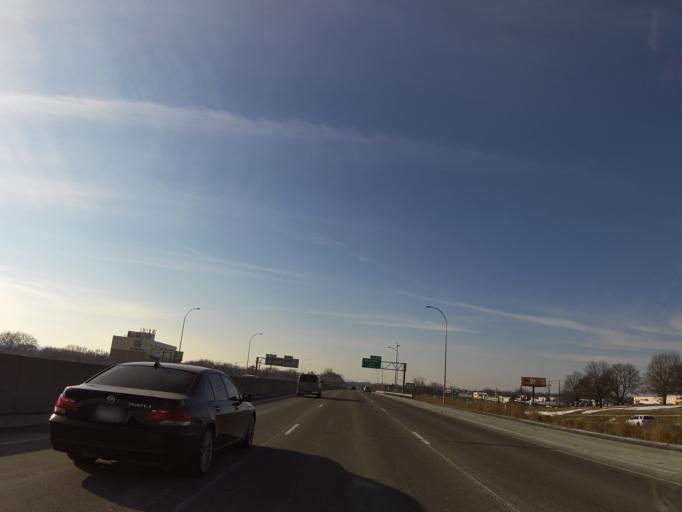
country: US
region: Minnesota
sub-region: Ramsey County
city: Maplewood
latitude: 44.9501
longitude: -93.0024
